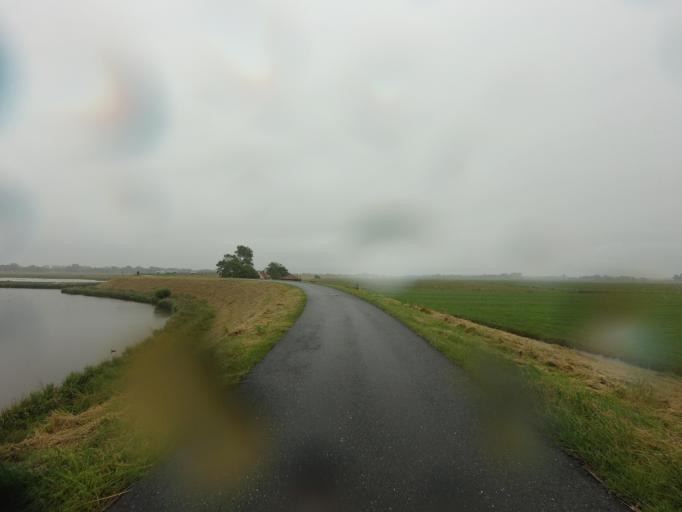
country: NL
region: North Holland
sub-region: Gemeente Schagen
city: Schagen
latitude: 52.8078
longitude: 4.7902
